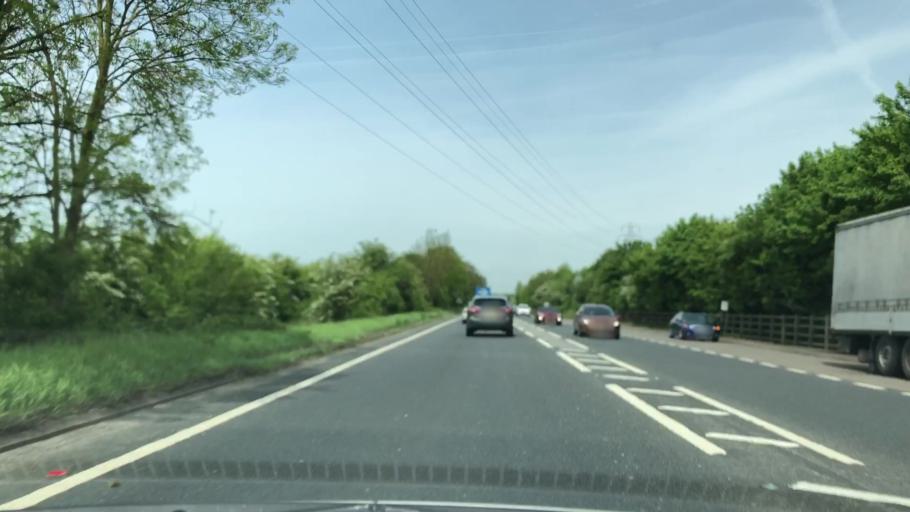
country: GB
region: England
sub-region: Shropshire
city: Gobowen
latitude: 52.9080
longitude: -3.0426
